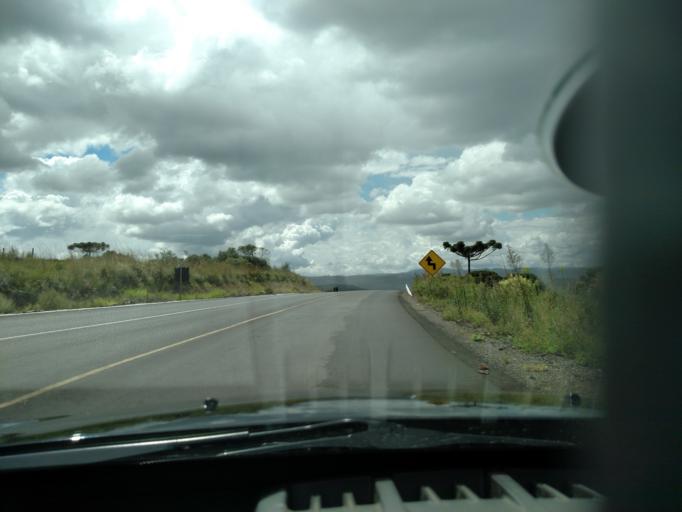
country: BR
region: Santa Catarina
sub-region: Sao Joaquim
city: Sao Joaquim
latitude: -28.1099
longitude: -50.0511
